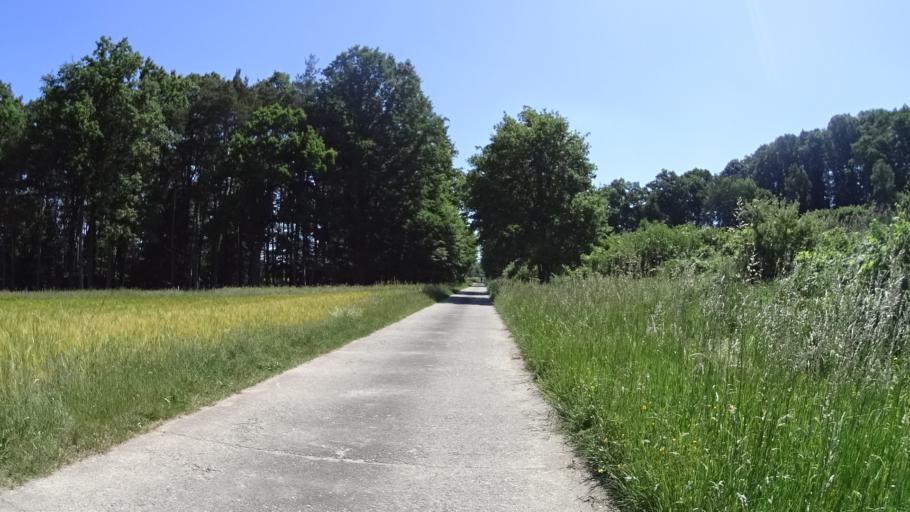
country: DE
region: Bavaria
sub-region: Regierungsbezirk Mittelfranken
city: Pfofeld
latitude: 49.1210
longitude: 10.8472
